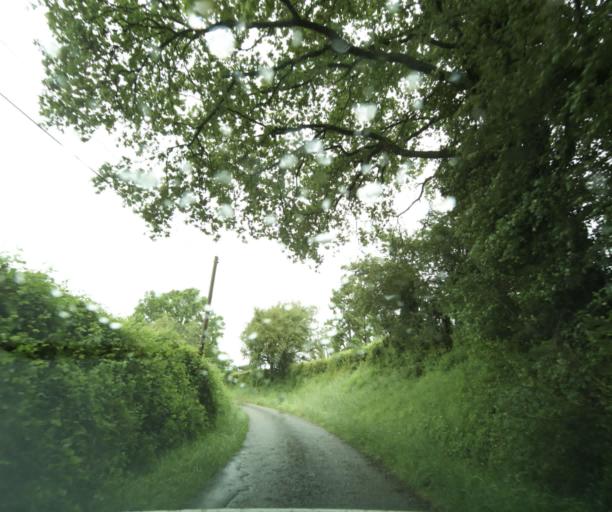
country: FR
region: Bourgogne
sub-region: Departement de Saone-et-Loire
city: Charolles
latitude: 46.5038
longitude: 4.3547
